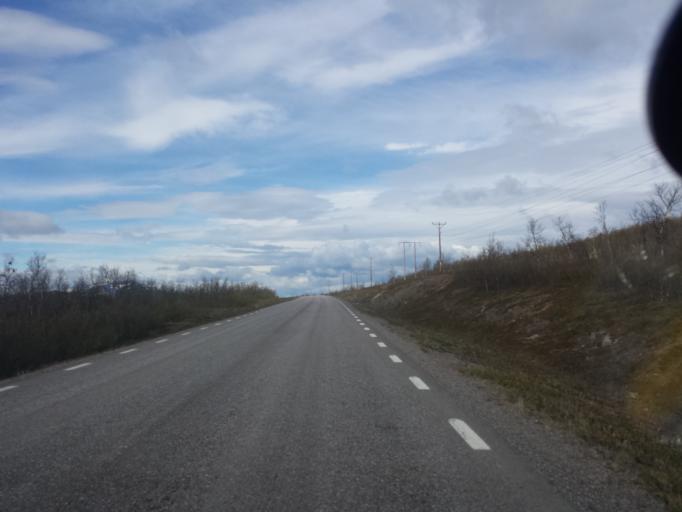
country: SE
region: Norrbotten
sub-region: Kiruna Kommun
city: Kiruna
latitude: 68.0457
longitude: 19.8303
